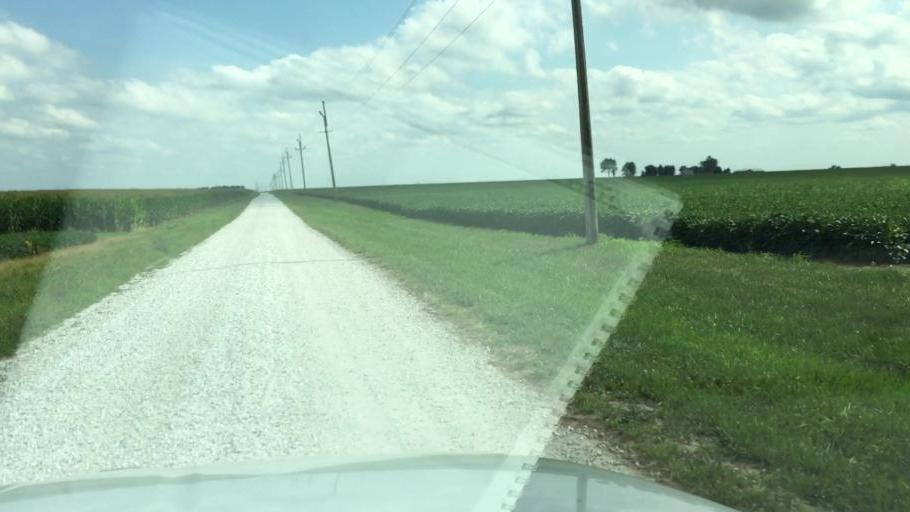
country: US
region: Illinois
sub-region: Hancock County
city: Carthage
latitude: 40.4130
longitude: -91.1785
